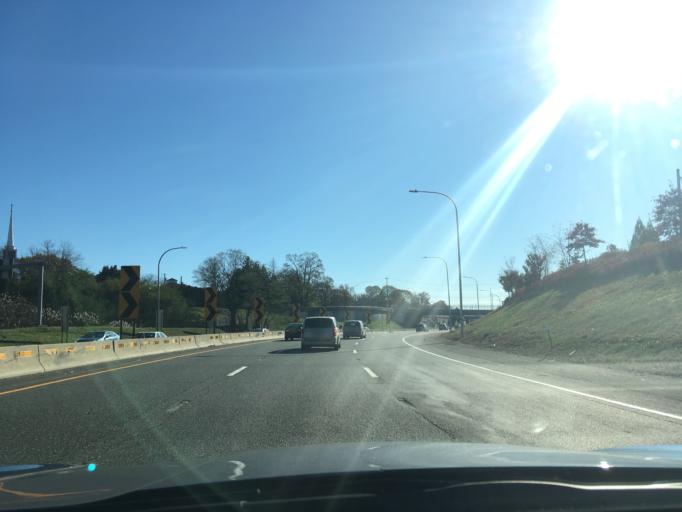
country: US
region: Rhode Island
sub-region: Providence County
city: Pawtucket
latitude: 41.8820
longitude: -71.3775
